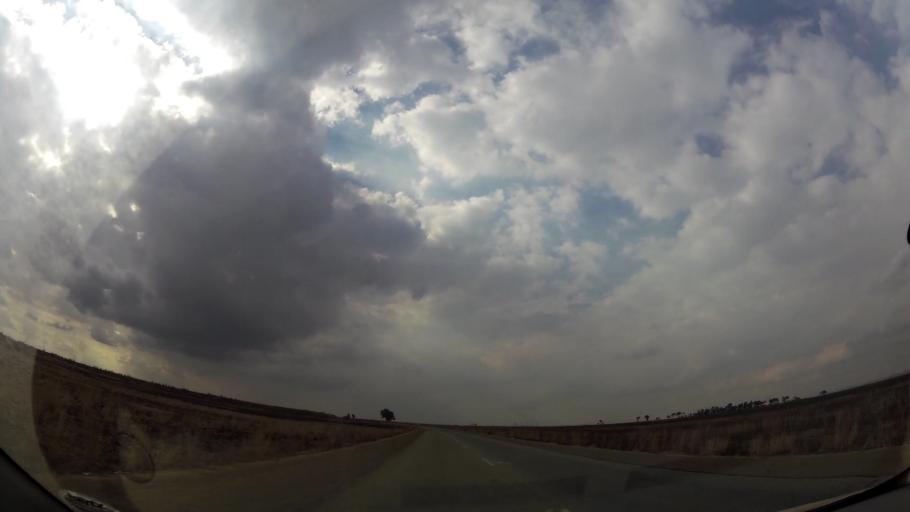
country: ZA
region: Orange Free State
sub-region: Fezile Dabi District Municipality
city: Sasolburg
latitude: -26.8804
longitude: 27.8859
